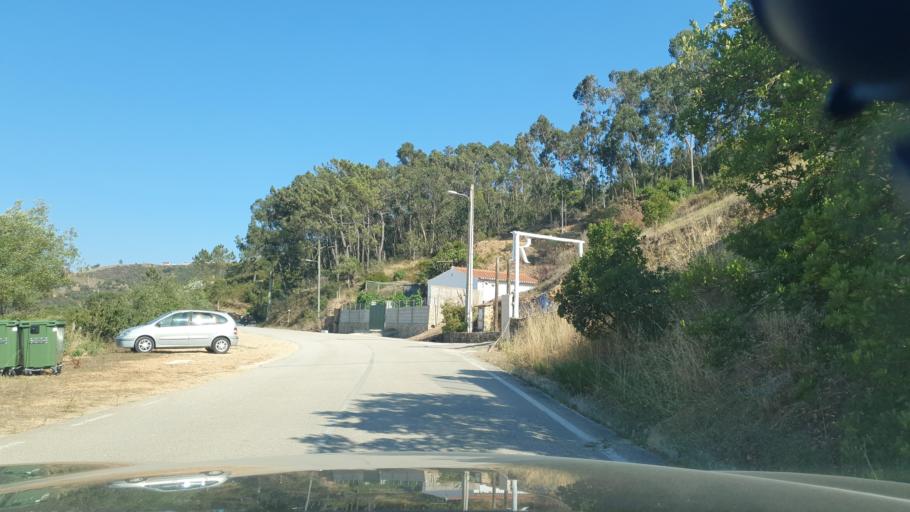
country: PT
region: Beja
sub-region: Odemira
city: Sao Teotonio
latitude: 37.4331
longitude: -8.7843
